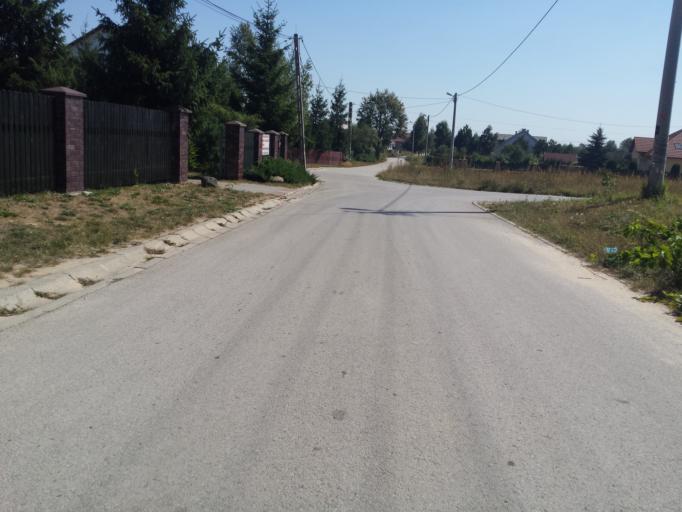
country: PL
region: Swietokrzyskie
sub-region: Powiat kielecki
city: Daleszyce
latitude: 50.8114
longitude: 20.7743
